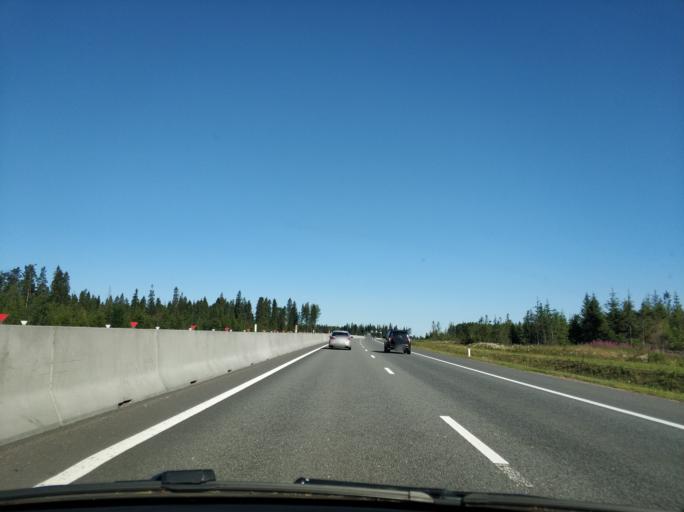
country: RU
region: Leningrad
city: Sosnovo
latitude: 60.4417
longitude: 30.2112
